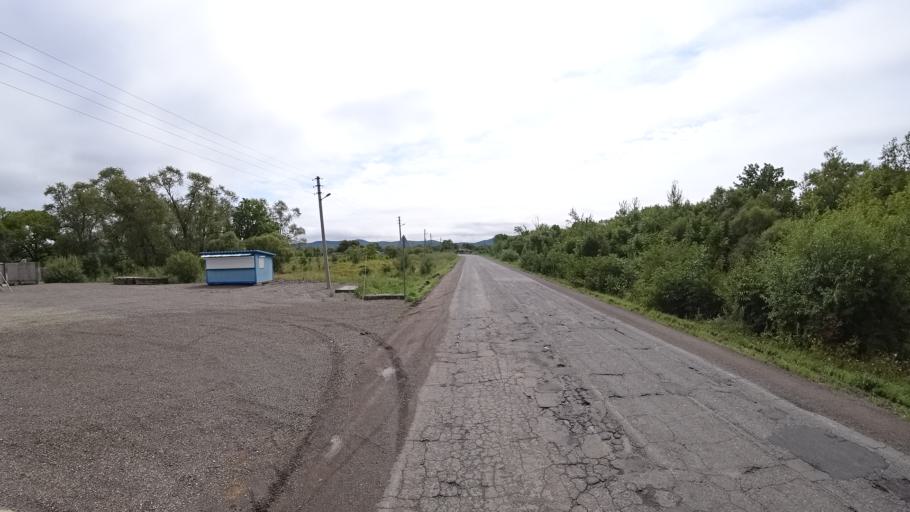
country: RU
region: Primorskiy
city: Monastyrishche
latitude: 44.1918
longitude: 132.4810
